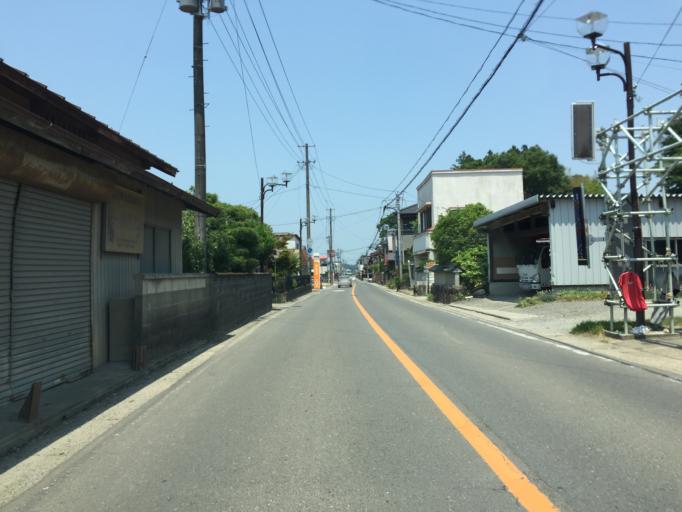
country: JP
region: Miyagi
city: Marumori
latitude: 37.8677
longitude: 140.8258
